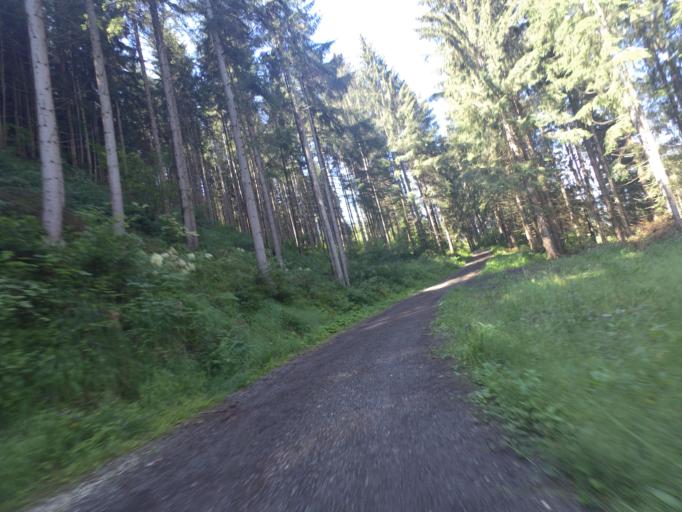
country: AT
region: Salzburg
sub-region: Politischer Bezirk Sankt Johann im Pongau
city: Schwarzach im Pongau
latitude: 47.3091
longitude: 13.1422
